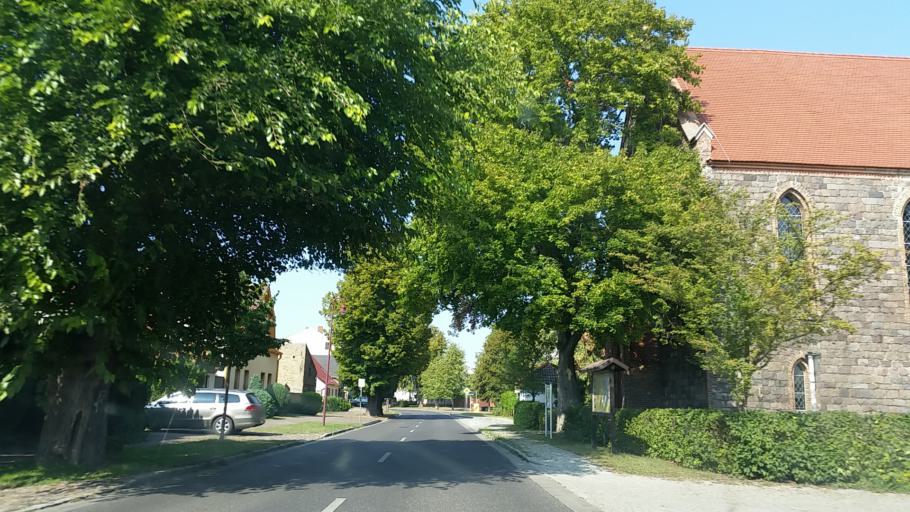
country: PL
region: West Pomeranian Voivodeship
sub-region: Powiat gryfinski
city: Cedynia
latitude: 52.8718
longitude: 14.1425
